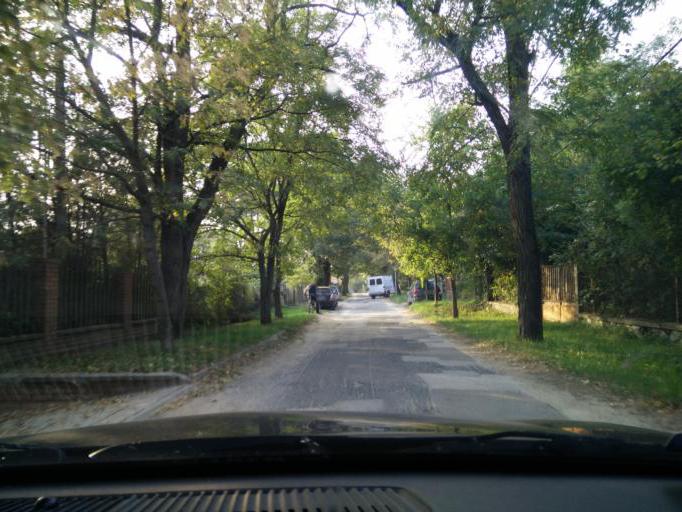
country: HU
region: Pest
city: Piliscsaba
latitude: 47.6412
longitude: 18.8348
